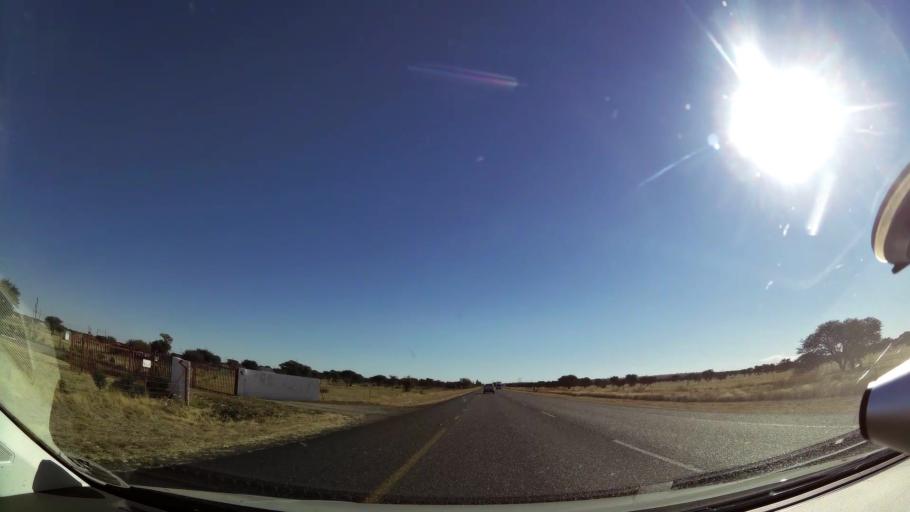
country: ZA
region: Northern Cape
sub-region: Frances Baard District Municipality
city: Kimberley
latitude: -28.6561
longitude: 24.7752
